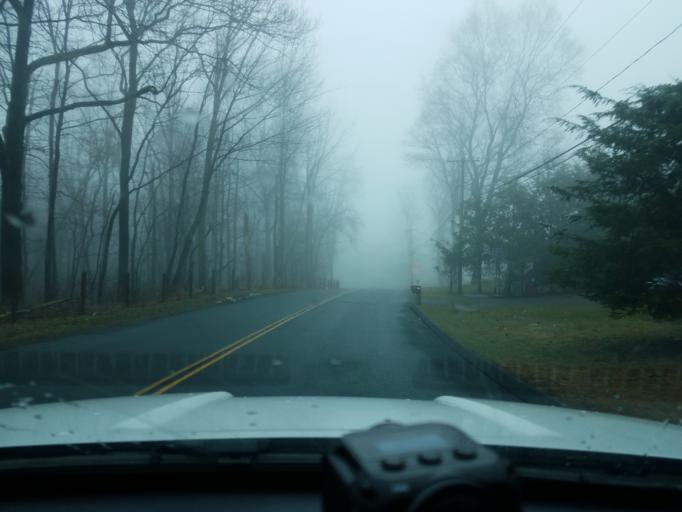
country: US
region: Connecticut
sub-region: New Haven County
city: Prospect
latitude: 41.4945
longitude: -73.0142
